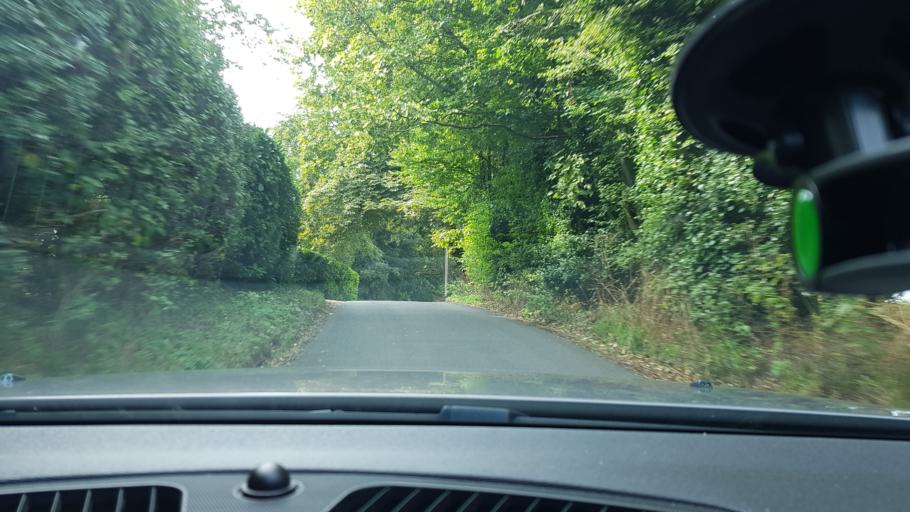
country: GB
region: England
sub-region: West Berkshire
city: Wickham
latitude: 51.4421
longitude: -1.4338
